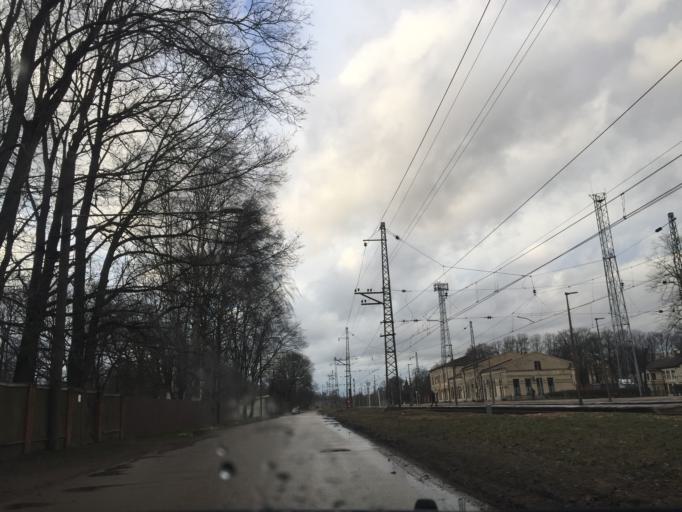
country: LV
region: Marupe
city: Marupe
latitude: 56.9402
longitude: 24.0525
